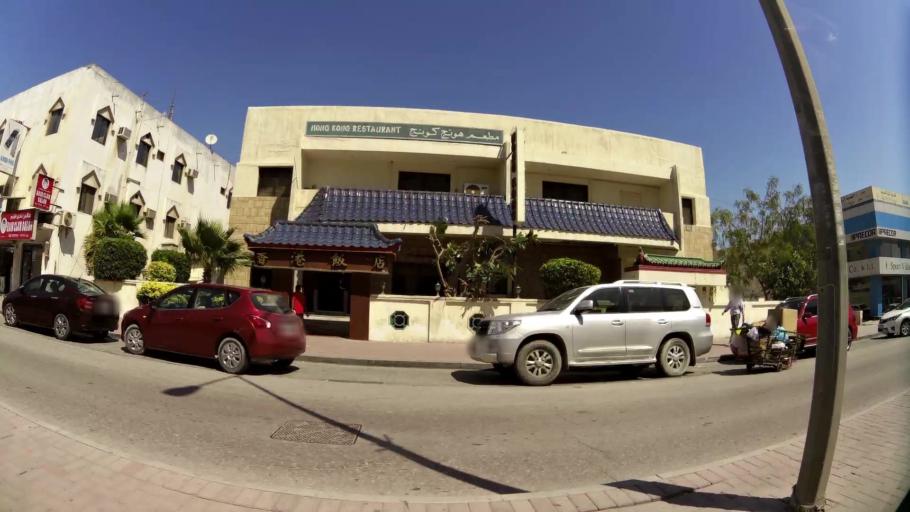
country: BH
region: Manama
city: Manama
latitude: 26.2044
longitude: 50.5964
